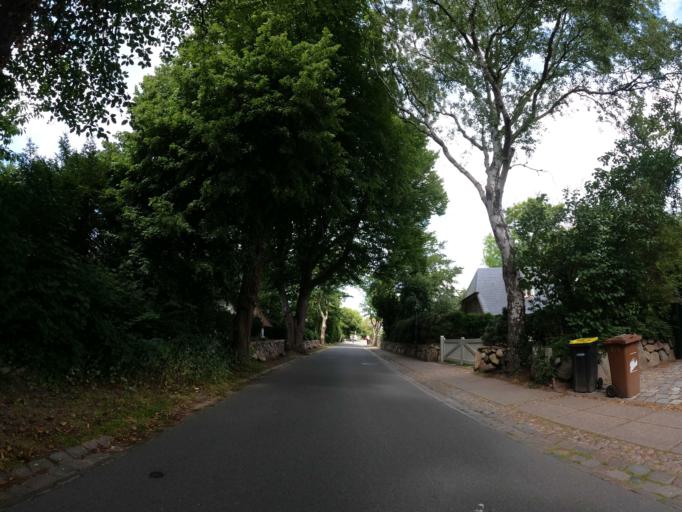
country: DE
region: Schleswig-Holstein
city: Keitum
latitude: 54.8922
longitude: 8.3704
